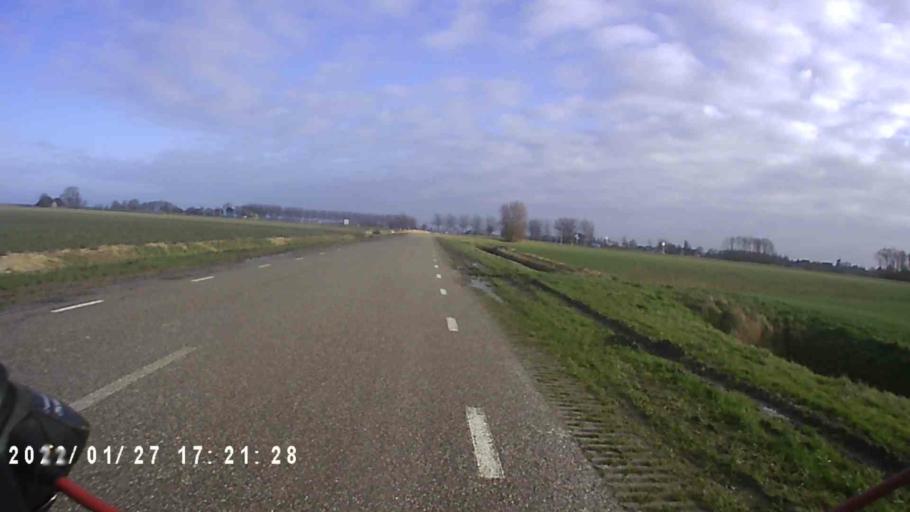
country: NL
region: Friesland
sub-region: Gemeente Dongeradeel
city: Anjum
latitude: 53.3820
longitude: 6.1210
